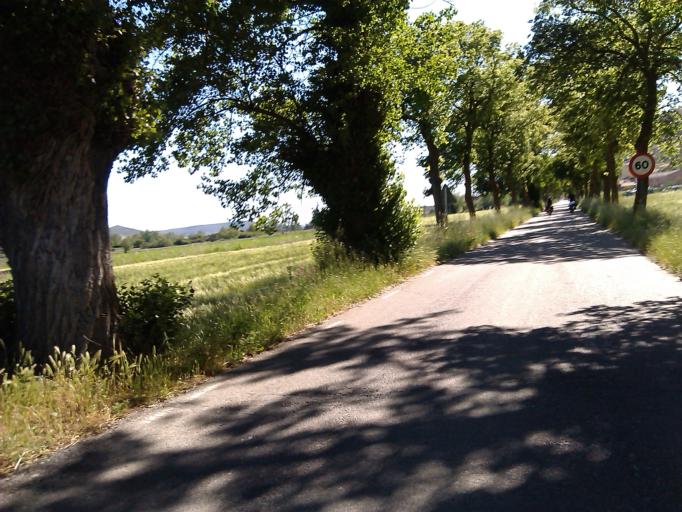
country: ES
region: Castille and Leon
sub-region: Provincia de Burgos
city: Villaquiran de la Puebla
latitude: 42.2920
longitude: -4.1254
